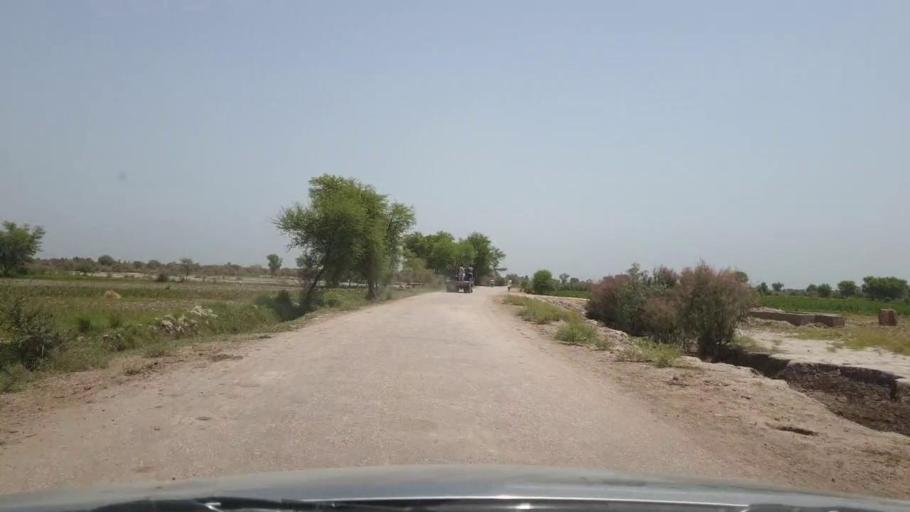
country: PK
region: Sindh
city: Pano Aqil
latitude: 27.8734
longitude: 69.1580
